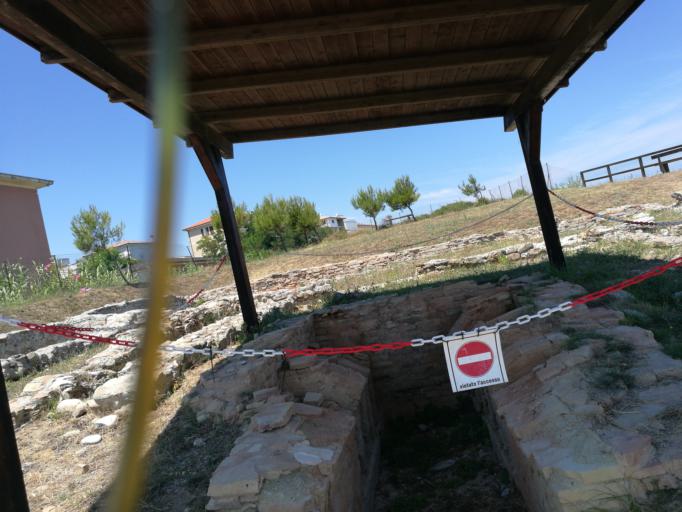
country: IT
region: Abruzzo
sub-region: Provincia di Chieti
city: Marina di San Vito
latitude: 42.3103
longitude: 14.4434
